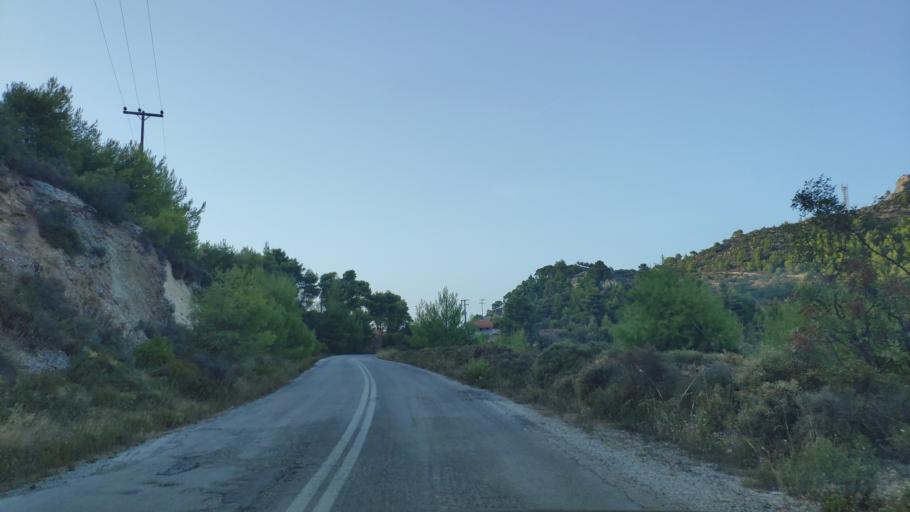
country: GR
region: West Greece
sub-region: Nomos Achaias
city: Aiyira
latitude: 38.0968
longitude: 22.4084
